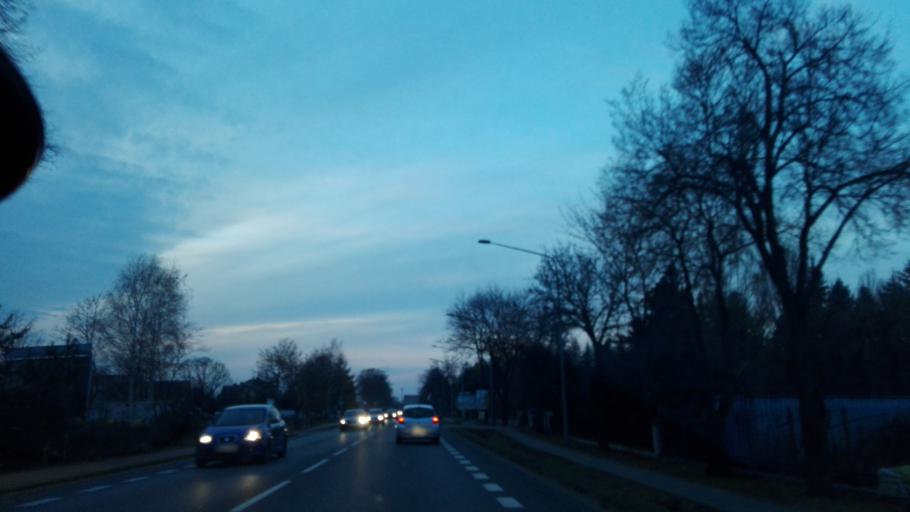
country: PL
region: Masovian Voivodeship
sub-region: Siedlce
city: Siedlce
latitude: 52.1748
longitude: 22.2005
